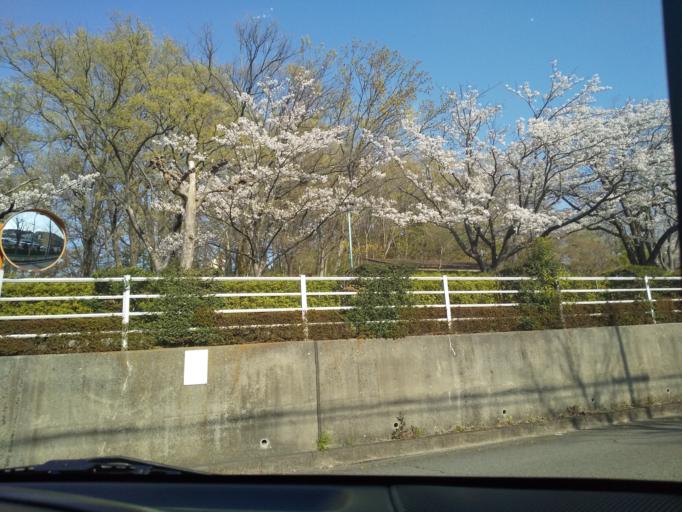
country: JP
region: Tokyo
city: Hino
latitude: 35.6525
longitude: 139.4222
